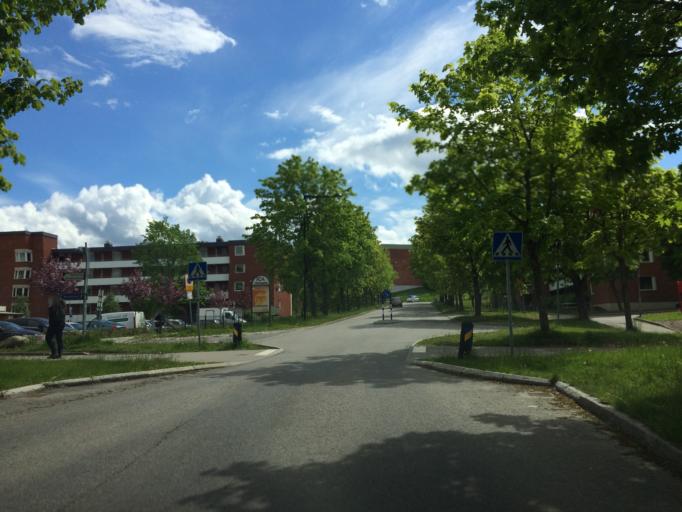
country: SE
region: Stockholm
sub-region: Botkyrka Kommun
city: Fittja
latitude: 59.2649
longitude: 17.8877
